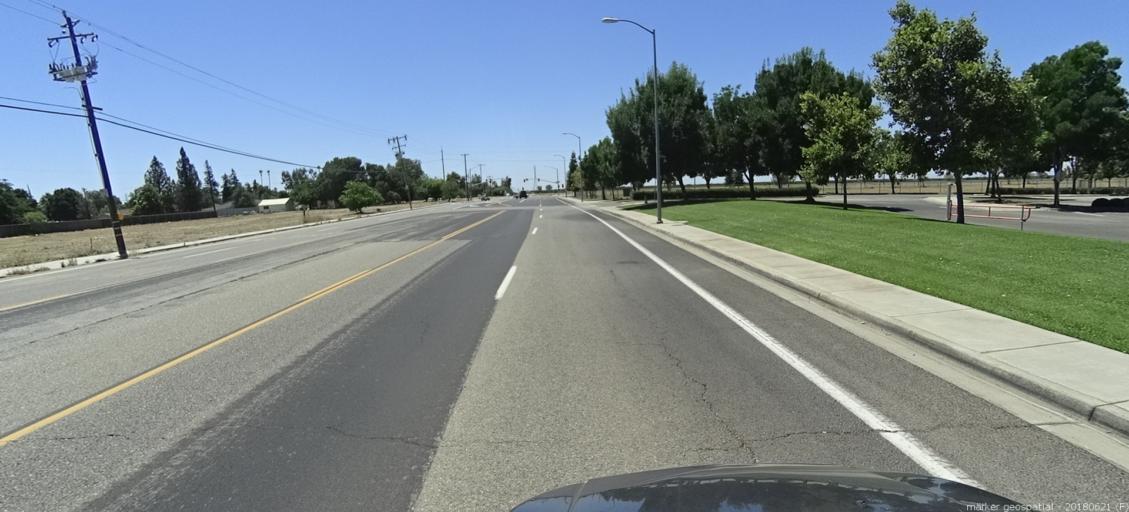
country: US
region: California
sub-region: Madera County
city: Bonadelle Ranchos-Madera Ranchos
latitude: 36.9249
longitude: -119.8944
